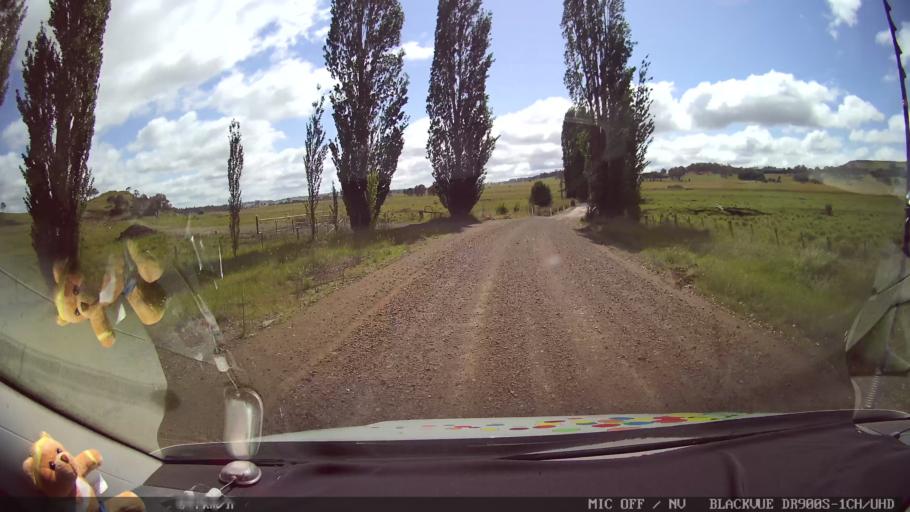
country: AU
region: New South Wales
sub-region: Glen Innes Severn
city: Glen Innes
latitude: -29.9444
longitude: 151.7117
